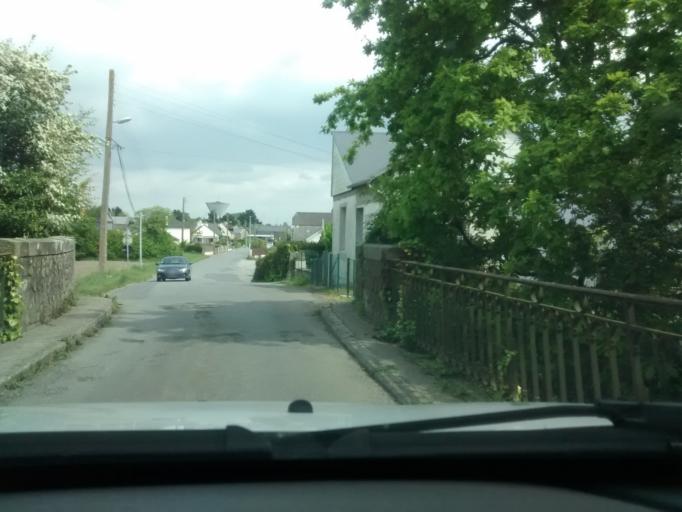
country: FR
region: Brittany
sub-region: Departement d'Ille-et-Vilaine
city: Dinard
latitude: 48.6175
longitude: -2.0640
